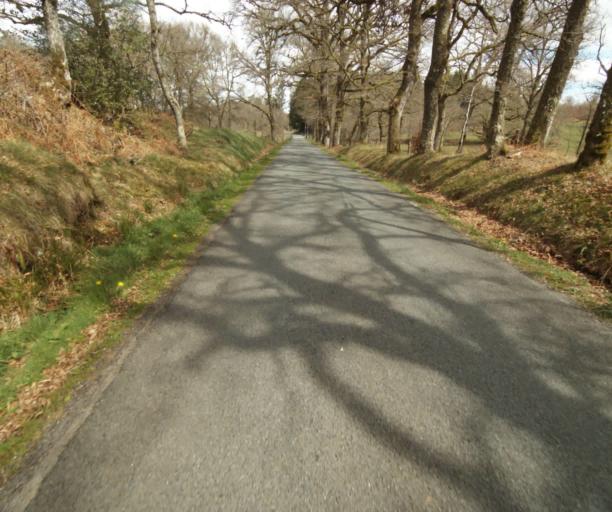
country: FR
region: Limousin
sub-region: Departement de la Correze
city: Correze
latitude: 45.3805
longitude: 1.9540
